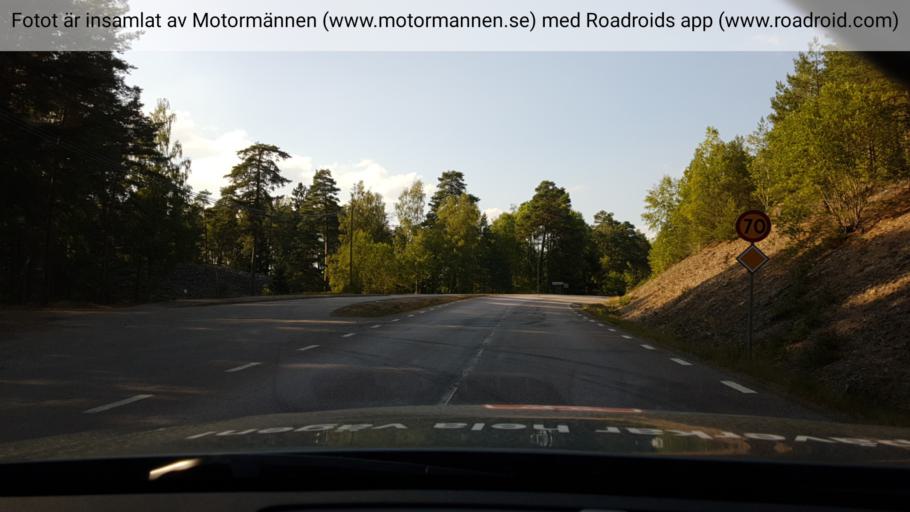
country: SE
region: Soedermanland
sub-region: Strangnas Kommun
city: Mariefred
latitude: 59.1702
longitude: 17.1857
